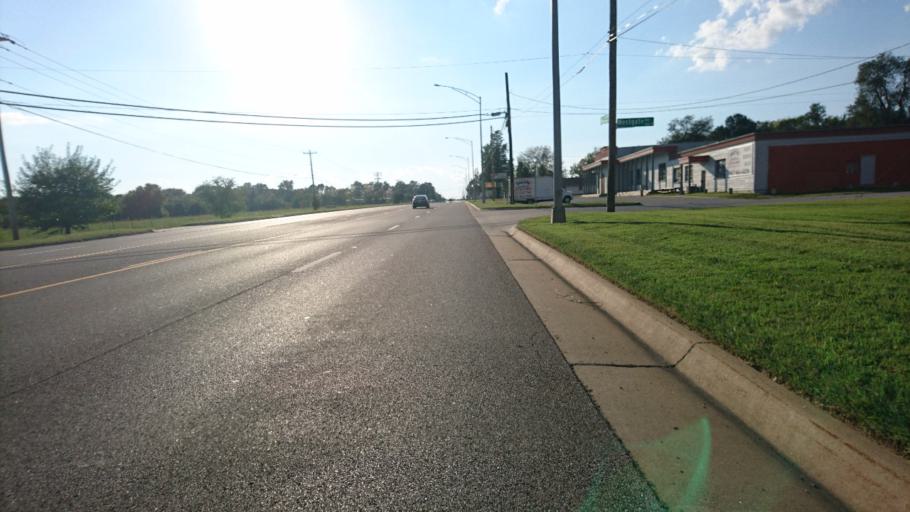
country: US
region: Missouri
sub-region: Greene County
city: Springfield
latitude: 37.2124
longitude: -93.3667
